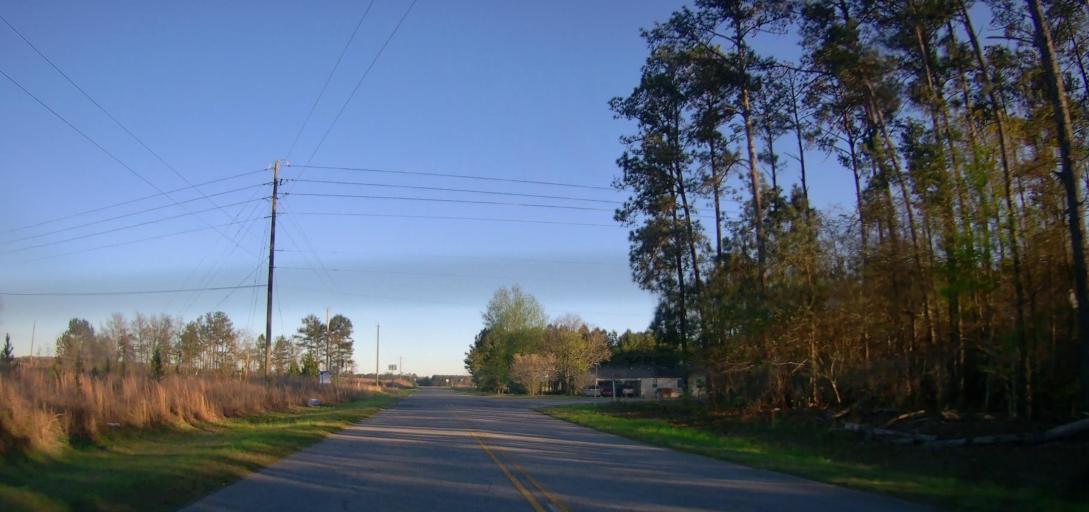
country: US
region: Georgia
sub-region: Wilkinson County
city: Gordon
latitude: 32.8896
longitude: -83.2988
